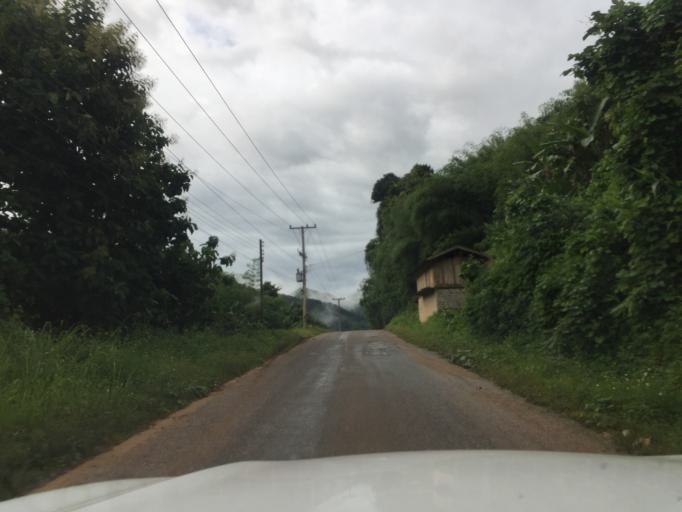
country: LA
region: Oudomxai
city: Muang La
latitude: 21.0864
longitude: 102.2421
